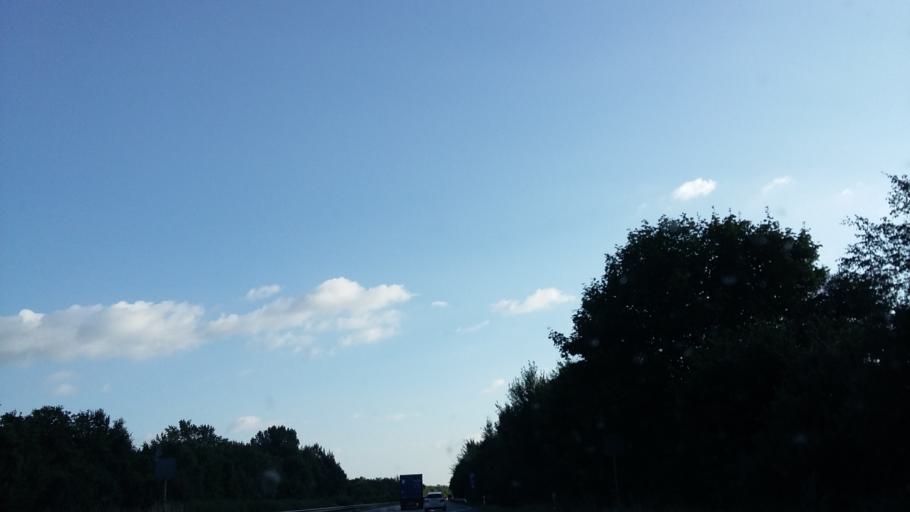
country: DE
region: Lower Saxony
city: Loxstedt
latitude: 53.4816
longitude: 8.6195
